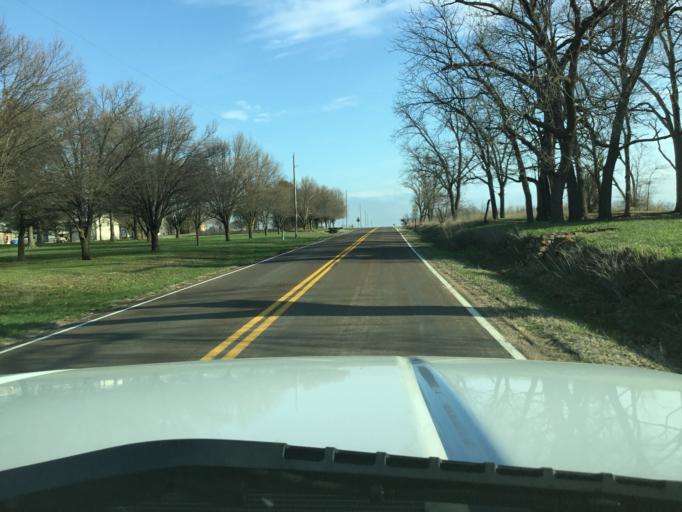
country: US
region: Kansas
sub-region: Shawnee County
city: Topeka
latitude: 39.1165
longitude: -95.7531
